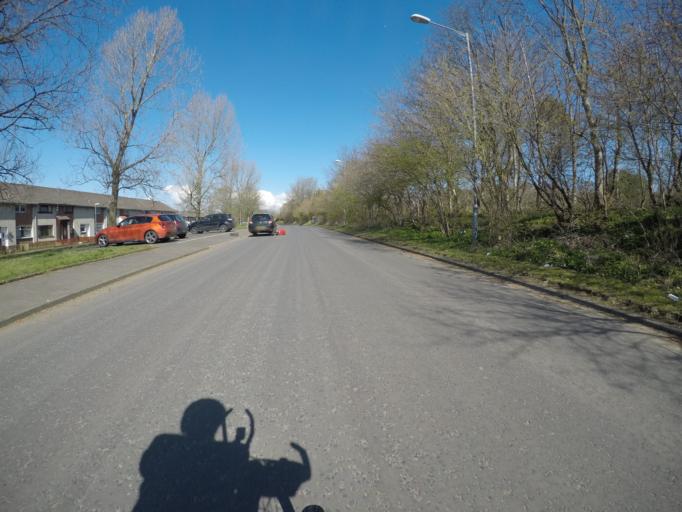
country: GB
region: Scotland
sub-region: North Ayrshire
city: Irvine
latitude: 55.6323
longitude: -4.6587
